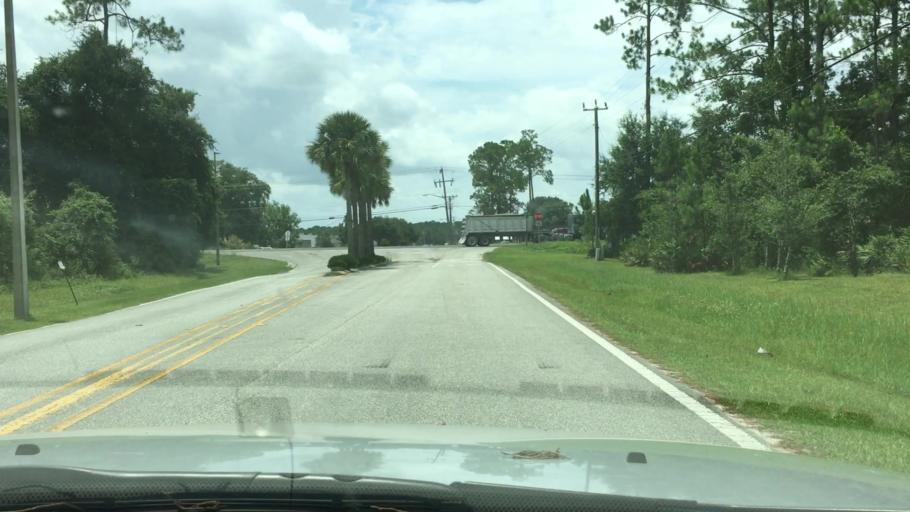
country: US
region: Florida
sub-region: Volusia County
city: Lake Helen
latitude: 29.0192
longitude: -81.2242
